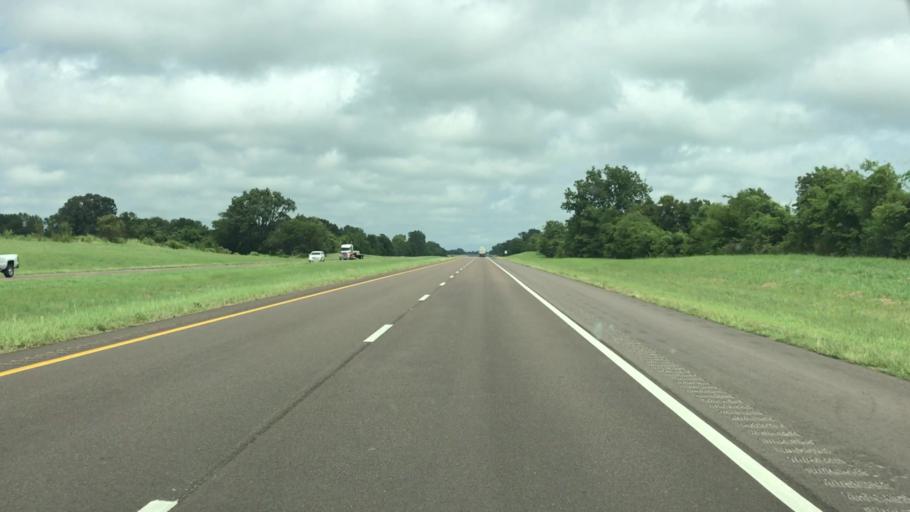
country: US
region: Tennessee
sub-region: Dyer County
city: Dyersburg
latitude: 36.0821
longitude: -89.3343
